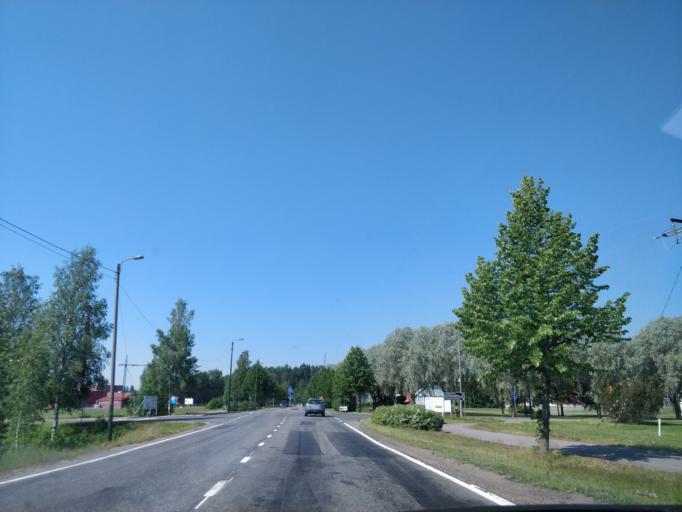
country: FI
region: Haeme
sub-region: Haemeenlinna
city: Tervakoski
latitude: 60.8173
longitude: 24.6366
